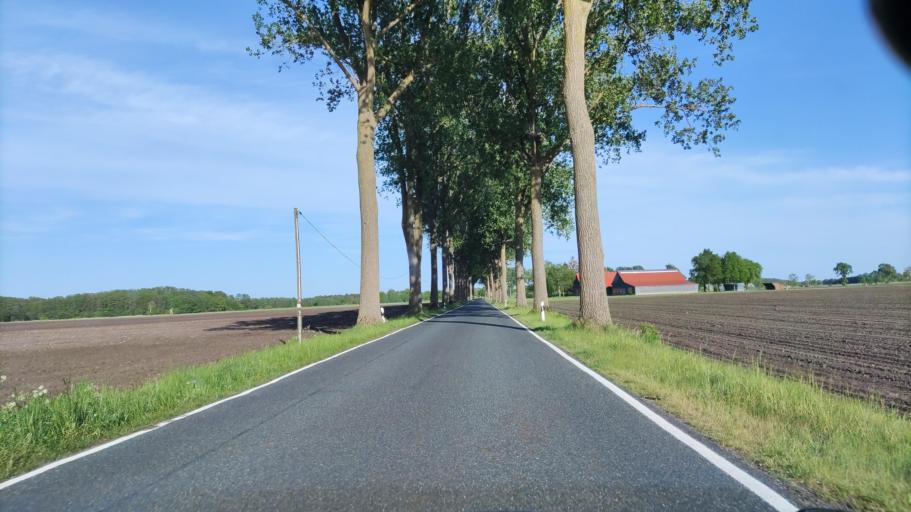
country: DE
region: Lower Saxony
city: Konigsmoor
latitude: 53.2217
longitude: 9.7062
